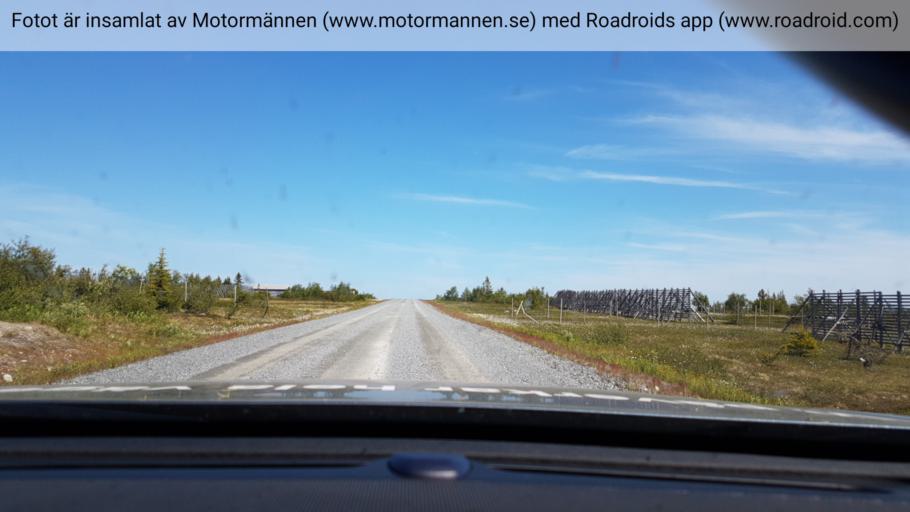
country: SE
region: Vaesterbotten
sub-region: Vilhelmina Kommun
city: Sjoberg
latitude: 64.7500
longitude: 15.8220
